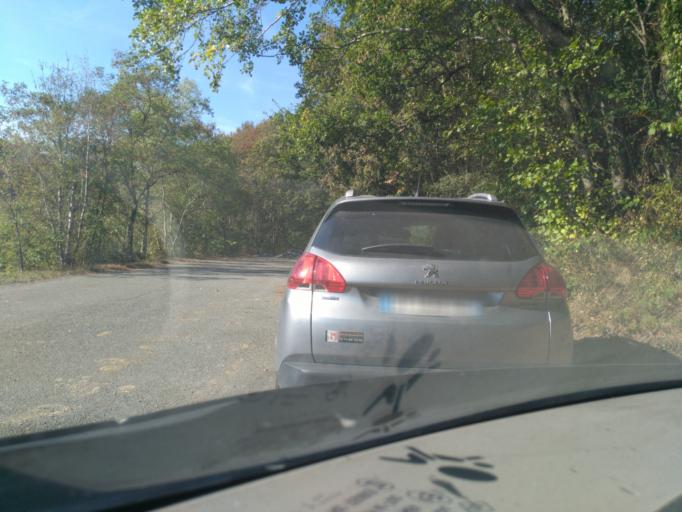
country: FR
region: Rhone-Alpes
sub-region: Departement du Rhone
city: Montrottier
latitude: 45.8303
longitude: 4.4179
